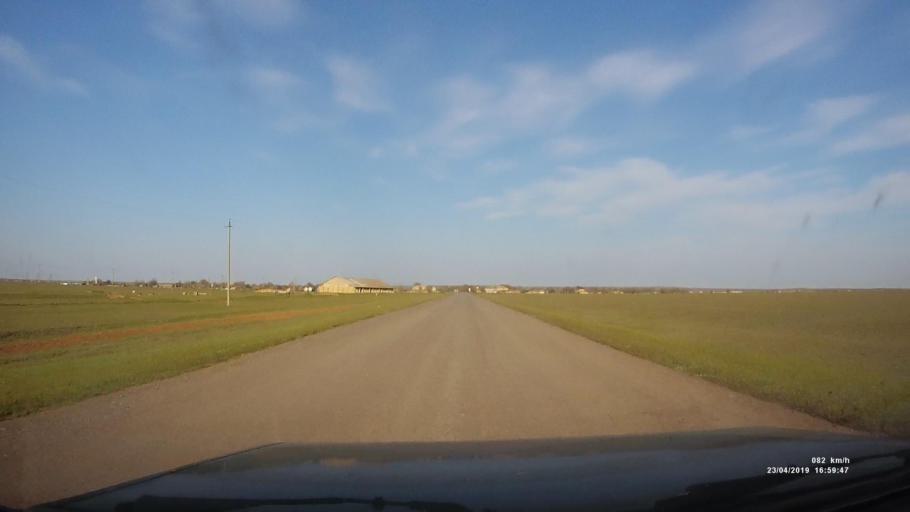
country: RU
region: Kalmykiya
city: Priyutnoye
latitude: 46.3080
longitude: 43.3968
